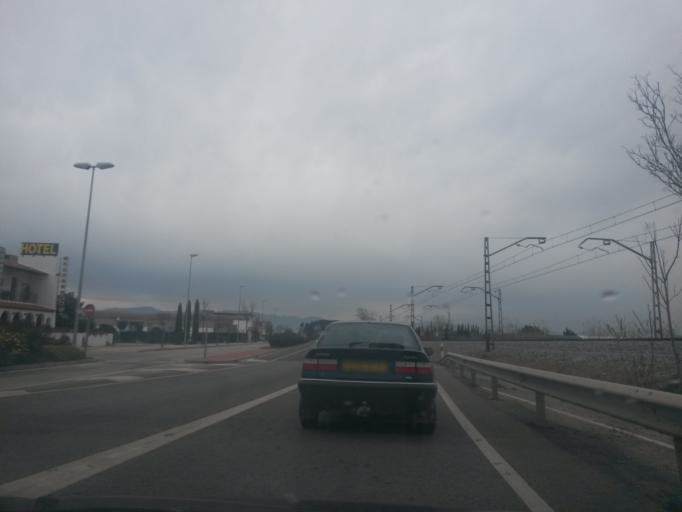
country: ES
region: Catalonia
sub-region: Provincia de Girona
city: Figueres
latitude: 42.2433
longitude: 2.9713
